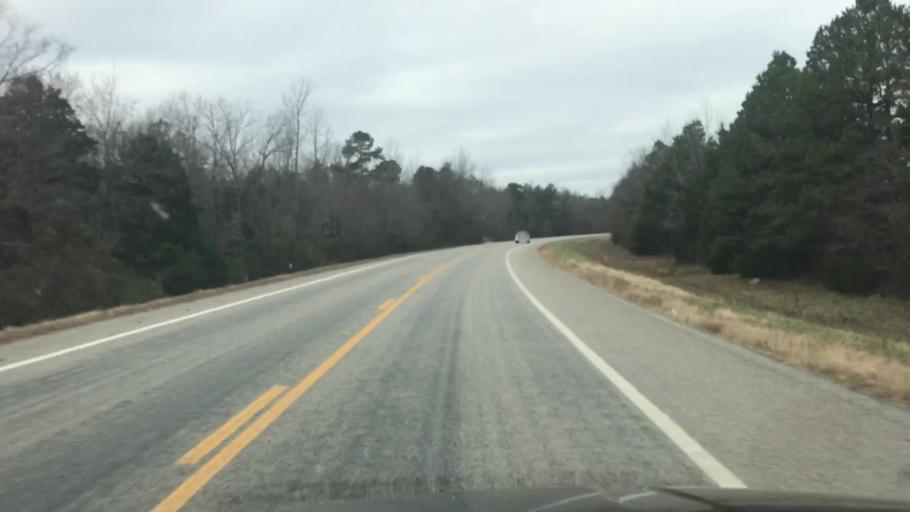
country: US
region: Arkansas
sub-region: Scott County
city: Waldron
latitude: 34.7040
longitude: -93.9260
